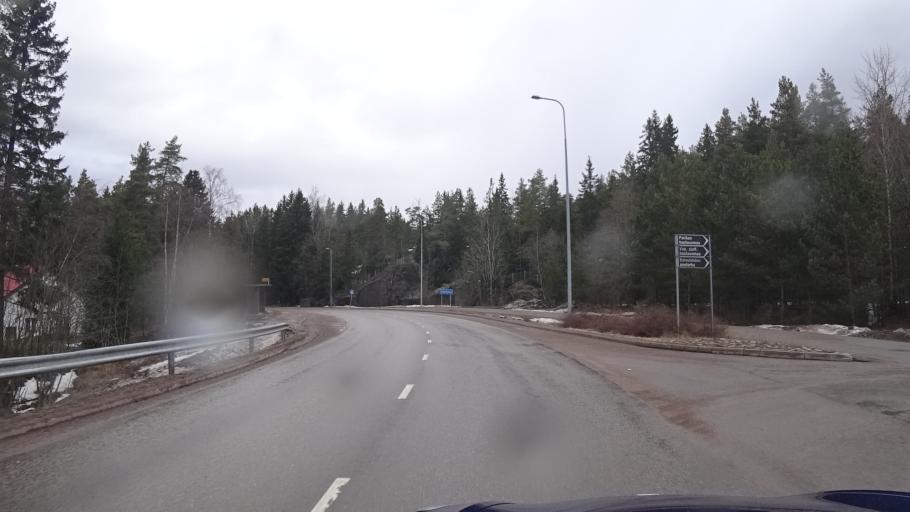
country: FI
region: Kymenlaakso
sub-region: Kotka-Hamina
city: Karhula
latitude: 60.5184
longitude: 26.8900
